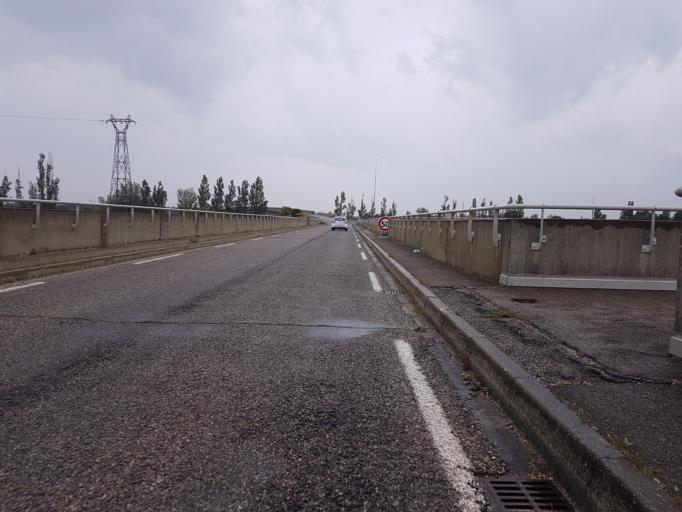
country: FR
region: Languedoc-Roussillon
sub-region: Departement du Gard
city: Villeneuve-les-Avignon
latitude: 43.9960
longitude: 4.8170
